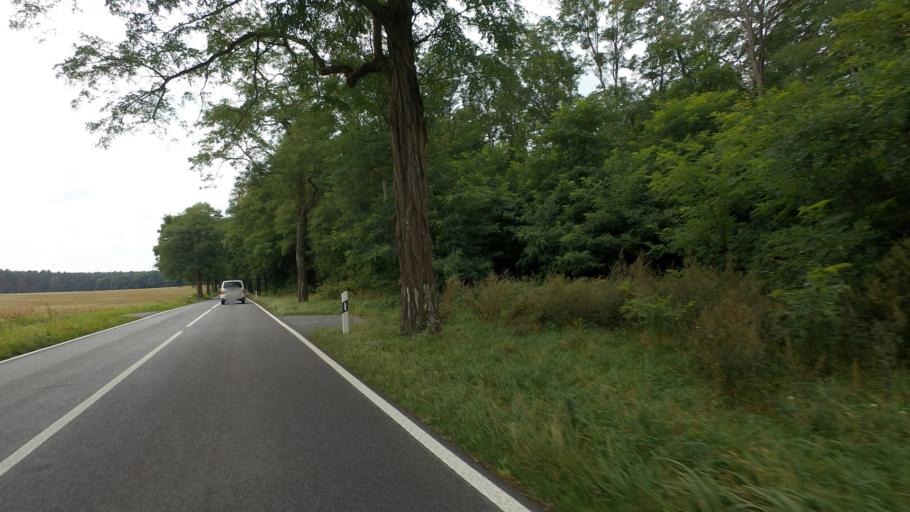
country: DE
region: Brandenburg
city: Baruth
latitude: 52.0299
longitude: 13.4777
